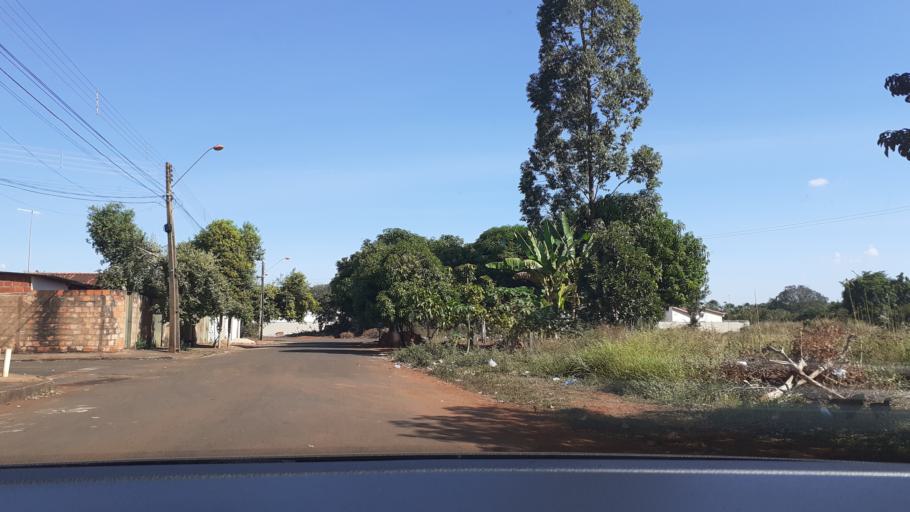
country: BR
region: Goias
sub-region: Itumbiara
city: Itumbiara
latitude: -18.4116
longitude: -49.2581
